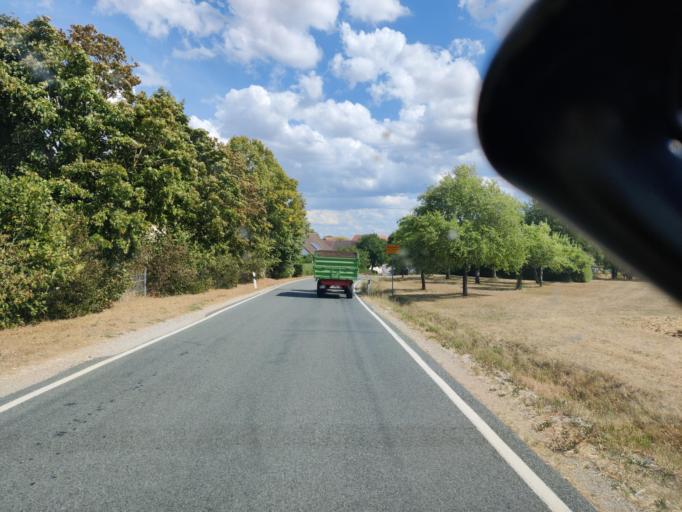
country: DE
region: Bavaria
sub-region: Regierungsbezirk Mittelfranken
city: Thalmassing
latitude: 49.0704
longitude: 11.2210
